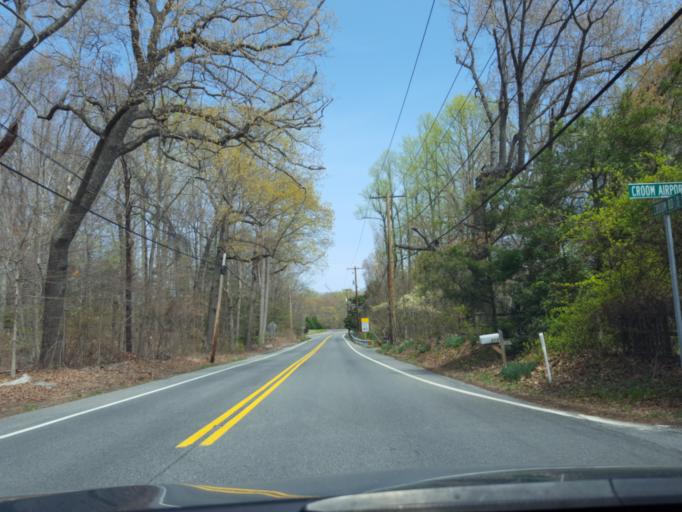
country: US
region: Maryland
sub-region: Prince George's County
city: Croom
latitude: 38.7608
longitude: -76.7591
